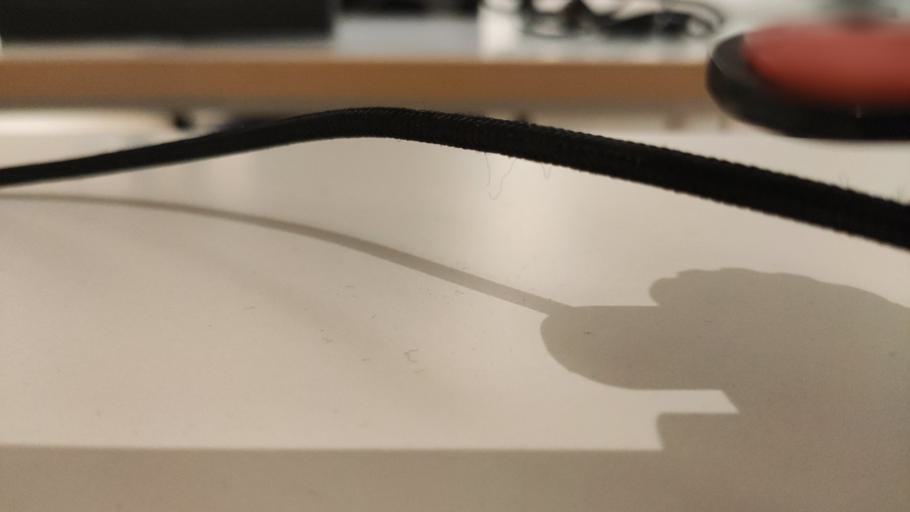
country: RU
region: Kaluga
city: Balabanovo
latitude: 55.1657
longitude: 36.6996
